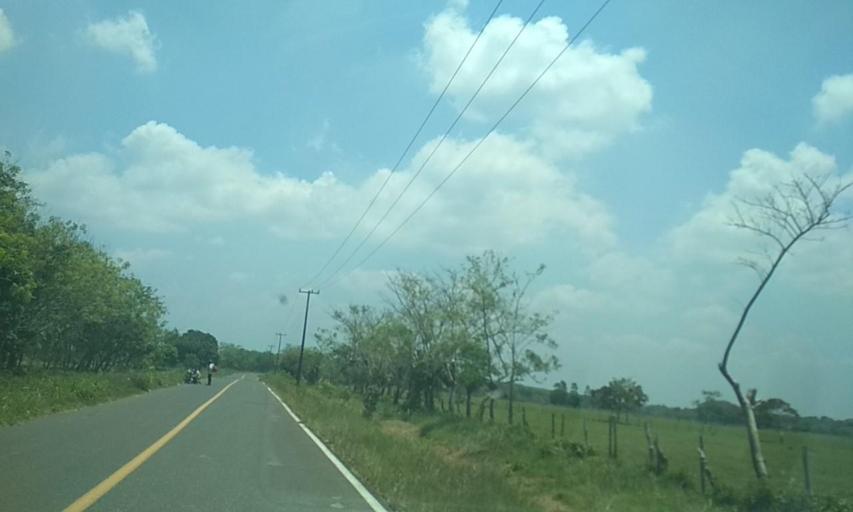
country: MX
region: Tabasco
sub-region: Huimanguillo
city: Francisco Rueda
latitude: 17.7580
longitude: -94.0538
